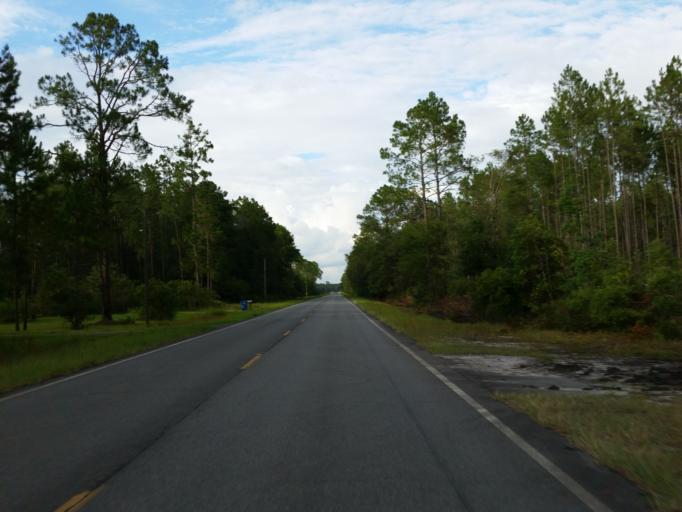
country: US
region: Florida
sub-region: Hamilton County
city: Jasper
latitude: 30.6483
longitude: -82.5710
